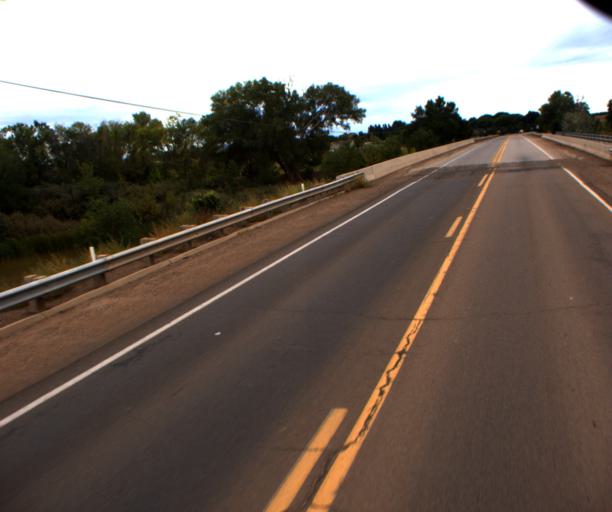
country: US
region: Arizona
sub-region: Navajo County
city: Snowflake
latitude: 34.5230
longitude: -110.0799
